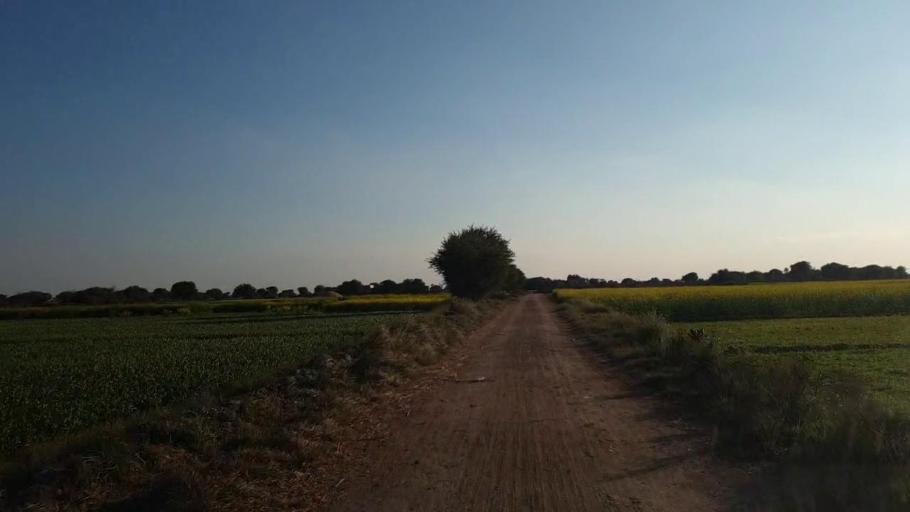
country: PK
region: Sindh
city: Shahpur Chakar
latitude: 26.1504
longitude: 68.5243
